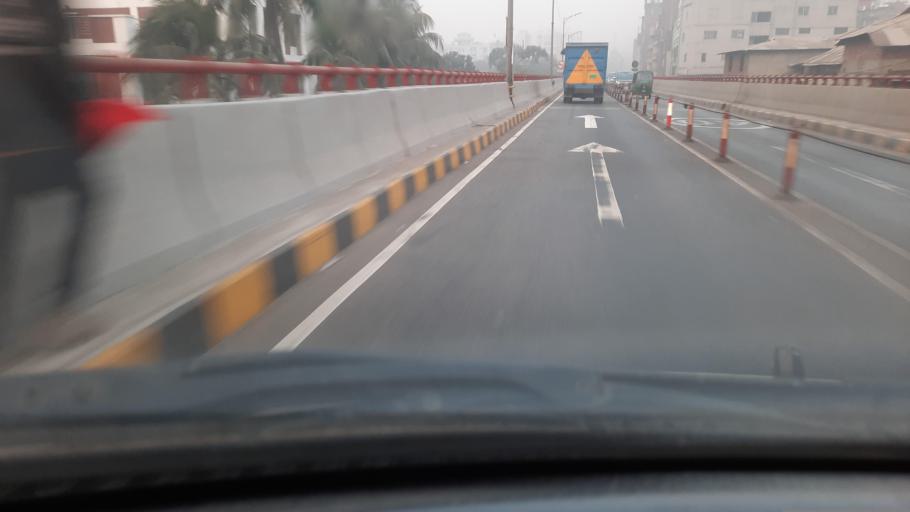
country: BD
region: Dhaka
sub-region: Dhaka
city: Dhaka
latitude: 23.7232
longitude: 90.4065
